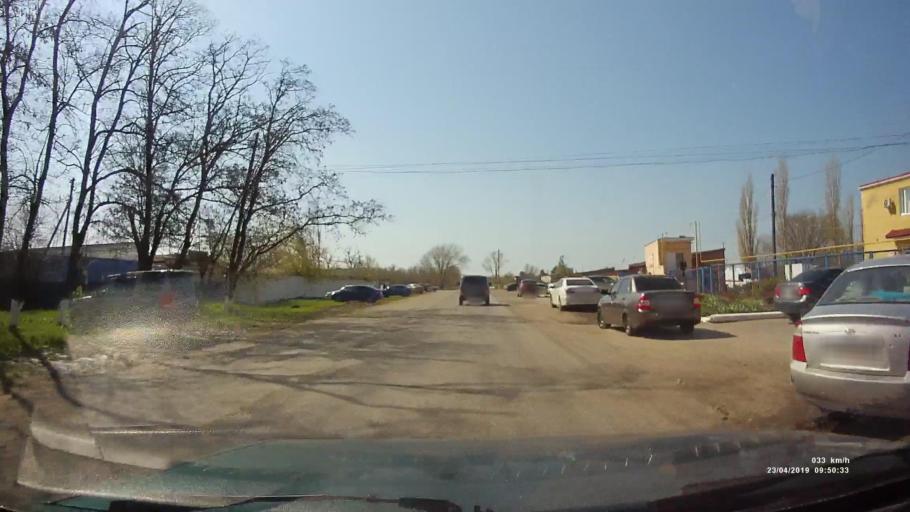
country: RU
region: Rostov
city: Orlovskiy
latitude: 46.8620
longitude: 42.0361
